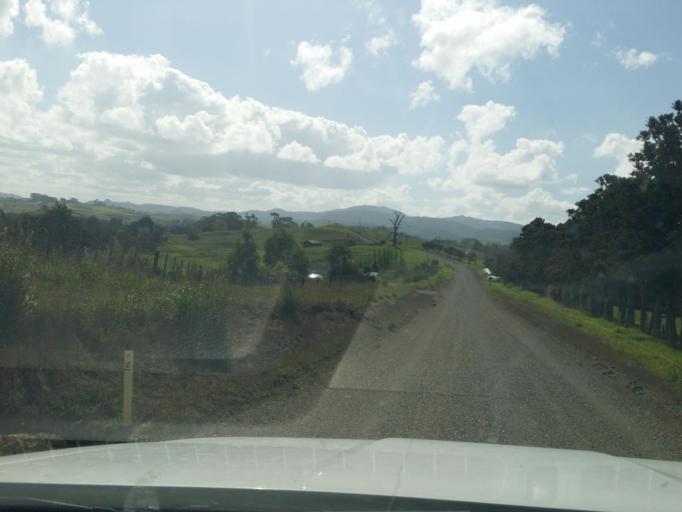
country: NZ
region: Auckland
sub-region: Auckland
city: Wellsford
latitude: -36.1546
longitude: 174.5214
